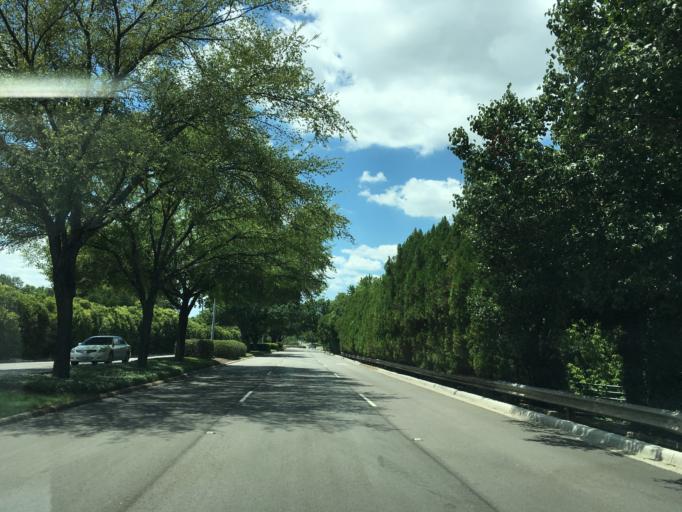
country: US
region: Texas
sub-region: Dallas County
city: Farmers Branch
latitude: 32.9243
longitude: -96.8614
